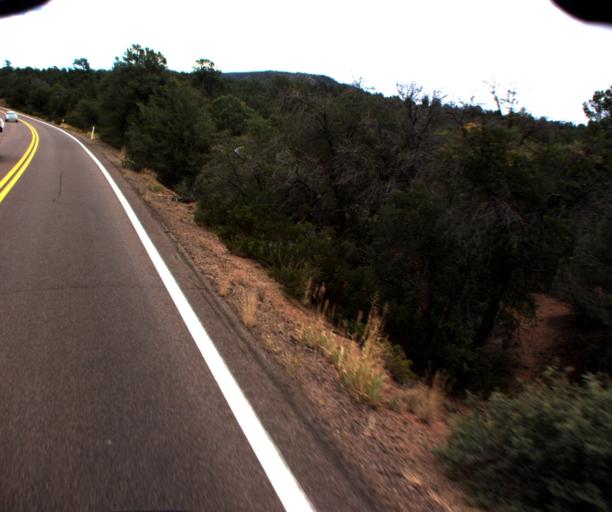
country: US
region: Arizona
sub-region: Gila County
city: Star Valley
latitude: 34.2613
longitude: -111.2056
